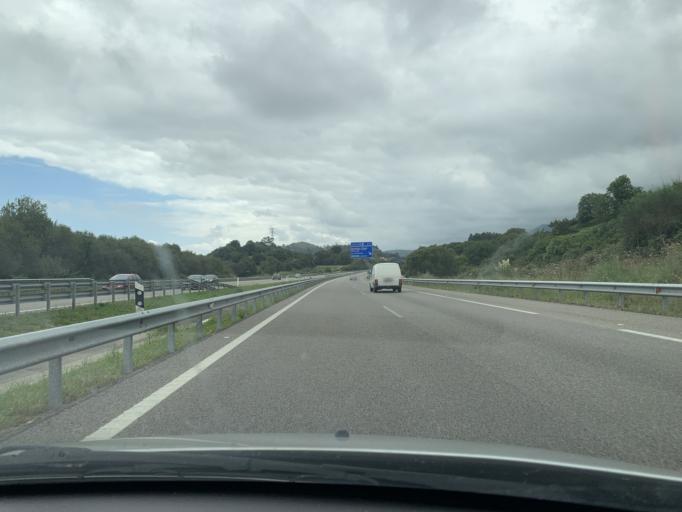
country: ES
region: Asturias
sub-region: Province of Asturias
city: Llanes
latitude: 43.4111
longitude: -4.7772
